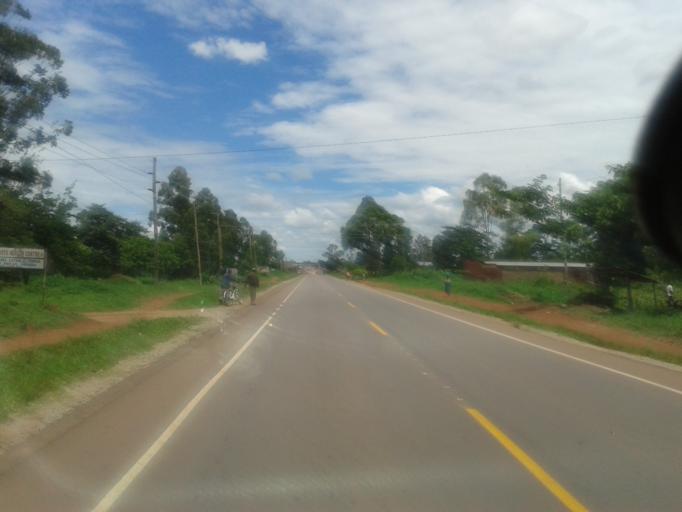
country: UG
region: Western Region
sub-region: Kiryandongo District
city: Kiryandongo
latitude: 1.8181
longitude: 32.0165
